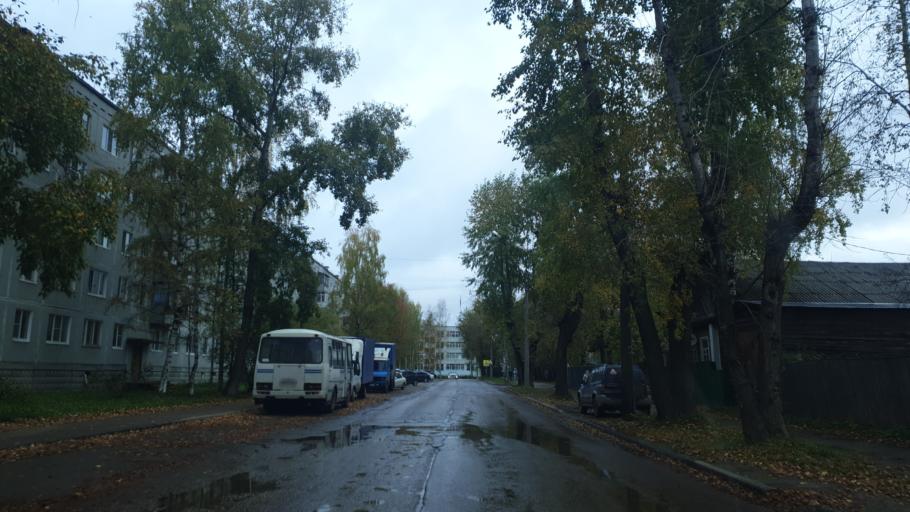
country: RU
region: Komi Republic
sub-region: Syktyvdinskiy Rayon
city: Syktyvkar
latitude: 61.6730
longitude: 50.8165
